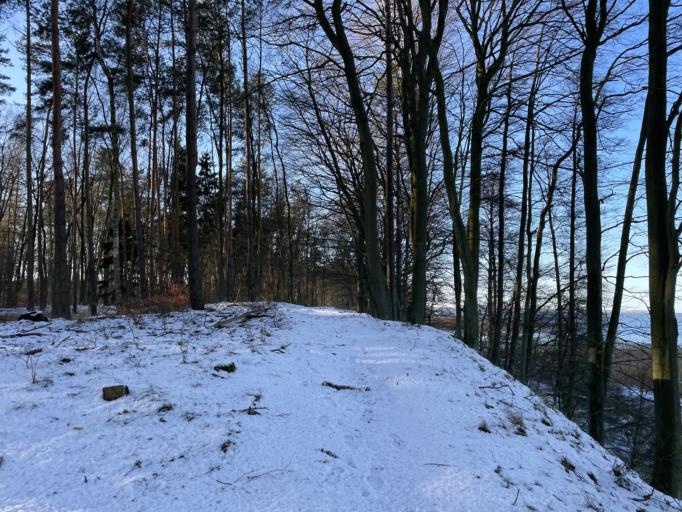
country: PL
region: West Pomeranian Voivodeship
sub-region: Powiat policki
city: Nowe Warpno
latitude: 53.6747
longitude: 14.4519
